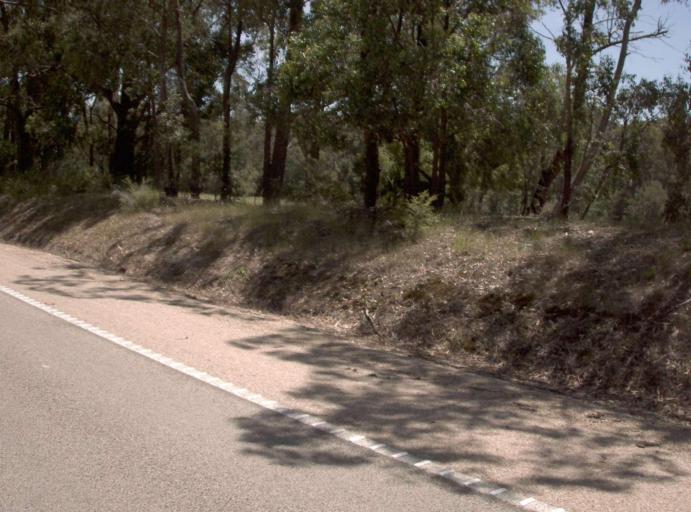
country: AU
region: Victoria
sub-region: East Gippsland
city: Bairnsdale
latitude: -37.7514
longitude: 147.7458
